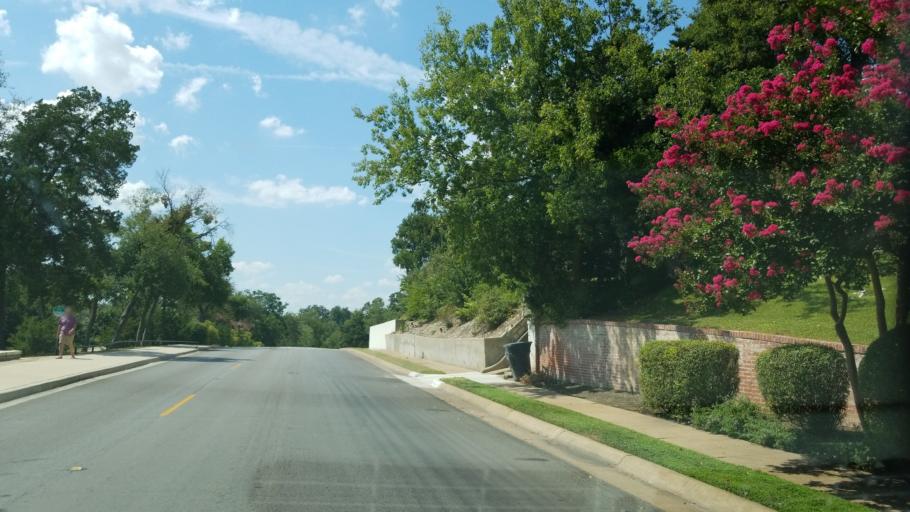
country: US
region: Texas
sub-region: Dallas County
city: Cockrell Hill
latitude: 32.7575
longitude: -96.8524
